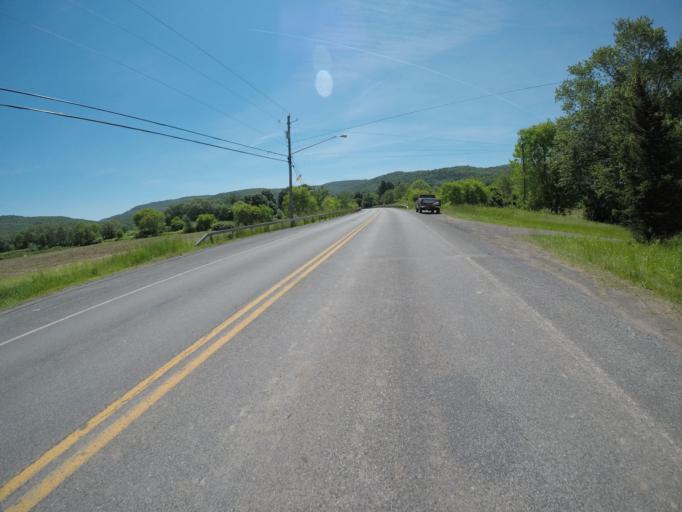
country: US
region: New York
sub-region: Delaware County
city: Delhi
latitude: 42.2092
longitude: -74.9772
